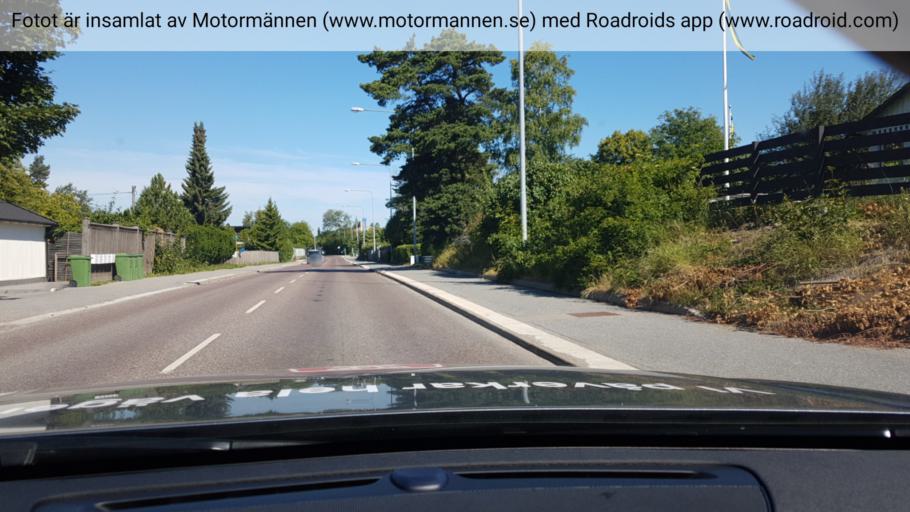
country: SE
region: Stockholm
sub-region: Huddinge Kommun
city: Segeltorp
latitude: 59.2694
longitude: 17.9565
